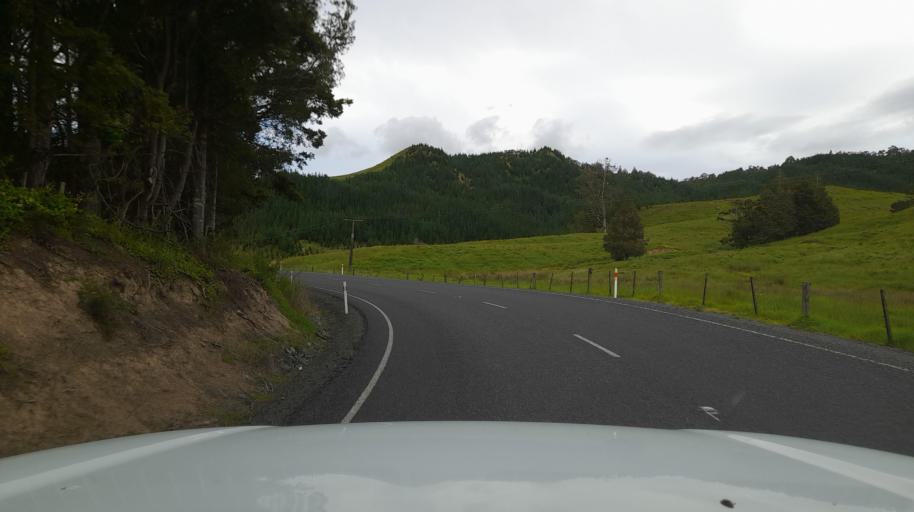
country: NZ
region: Northland
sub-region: Far North District
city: Kaitaia
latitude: -35.2986
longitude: 173.3648
